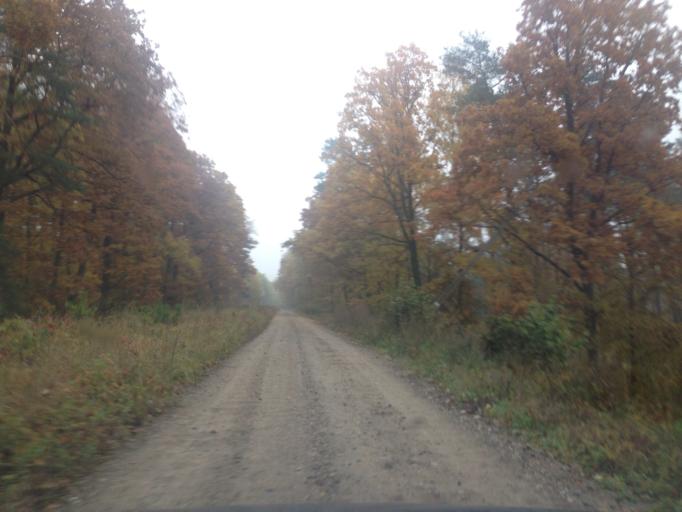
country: PL
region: Kujawsko-Pomorskie
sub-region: Powiat brodnicki
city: Gorzno
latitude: 53.2397
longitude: 19.6853
